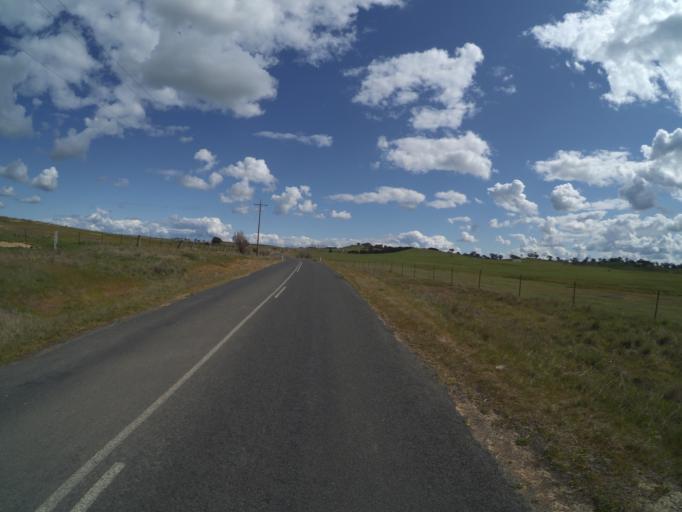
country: AU
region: New South Wales
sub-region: Yass Valley
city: Yass
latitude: -34.8789
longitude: 148.8983
